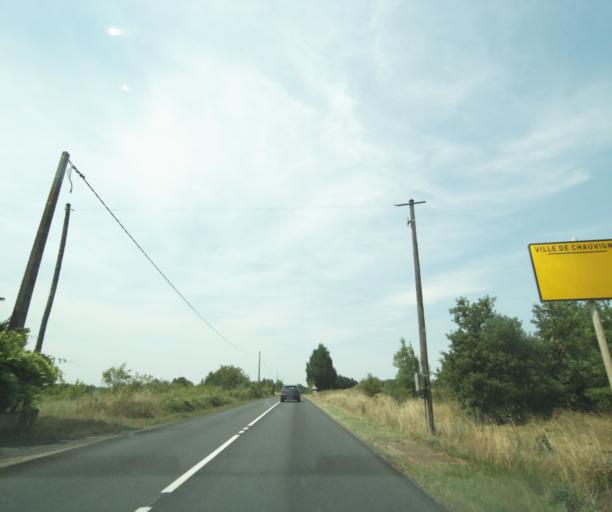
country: FR
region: Poitou-Charentes
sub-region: Departement de la Vienne
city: Chauvigny
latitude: 46.5476
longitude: 0.6414
